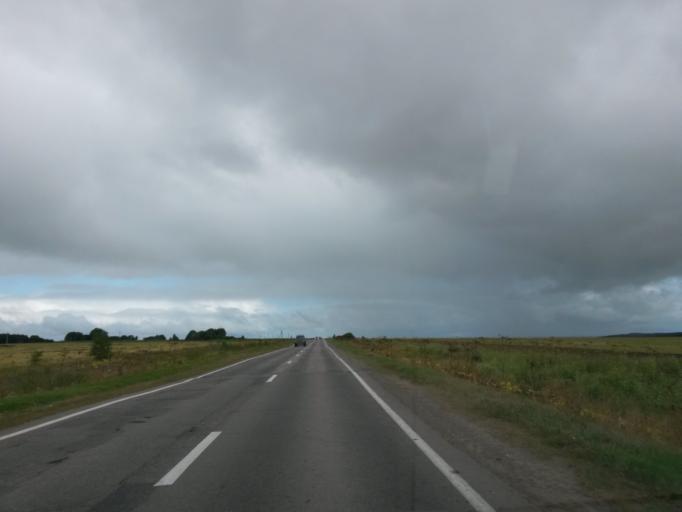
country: RU
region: Jaroslavl
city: Yaroslavl
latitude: 57.7533
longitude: 39.8744
